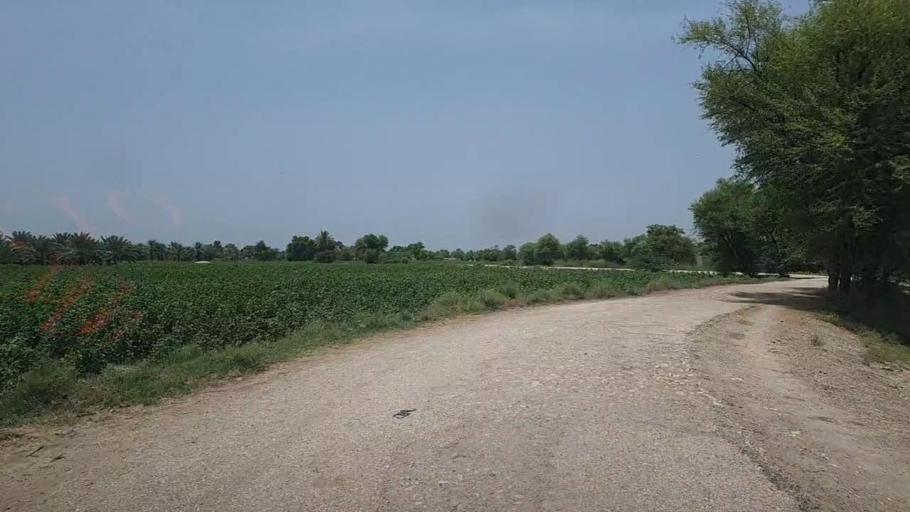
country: PK
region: Sindh
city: Pano Aqil
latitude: 27.8262
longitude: 69.2138
